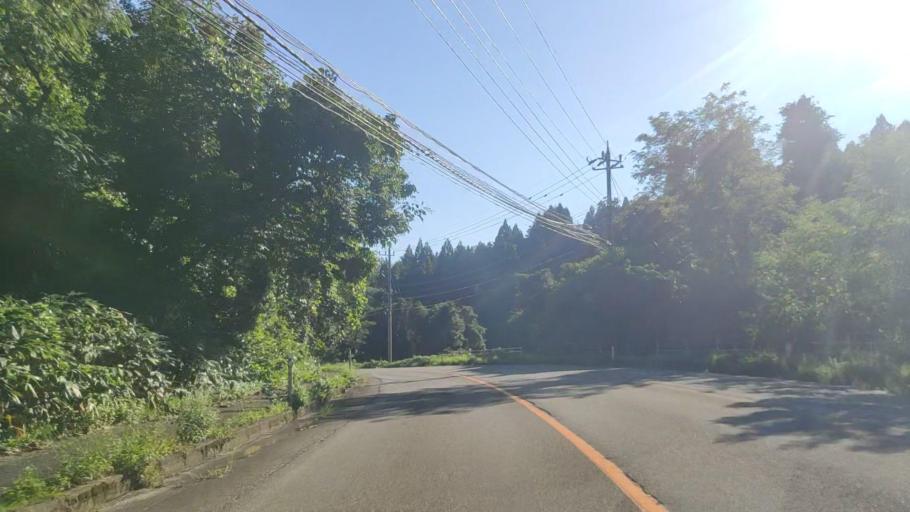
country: JP
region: Ishikawa
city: Nanao
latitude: 37.1230
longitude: 136.8626
